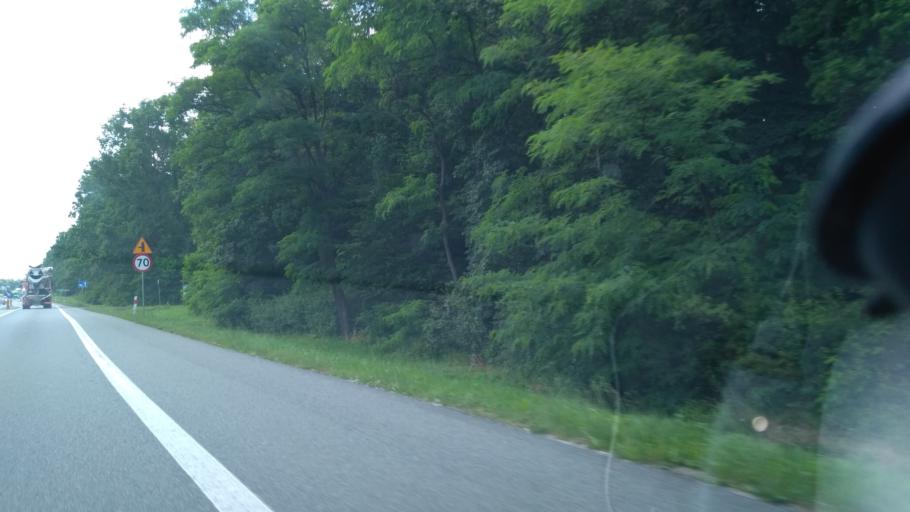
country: PL
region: Subcarpathian Voivodeship
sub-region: Powiat rzeszowski
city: Glogow Malopolski
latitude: 50.1252
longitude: 21.9692
